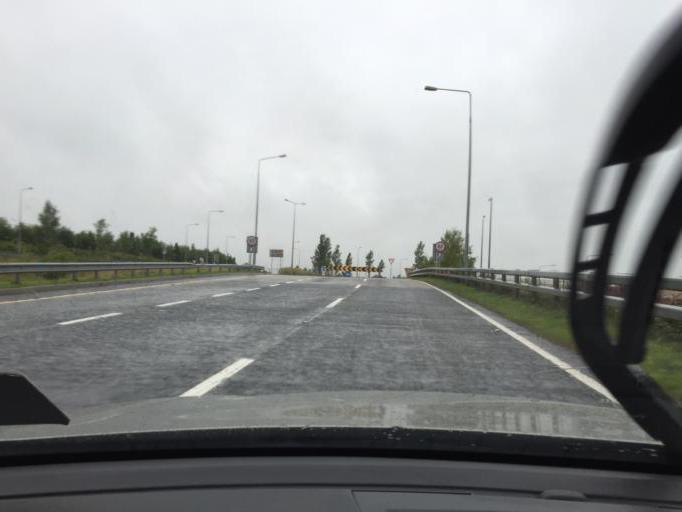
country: IE
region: Leinster
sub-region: Kildare
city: Celbridge
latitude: 53.3593
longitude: -6.5305
